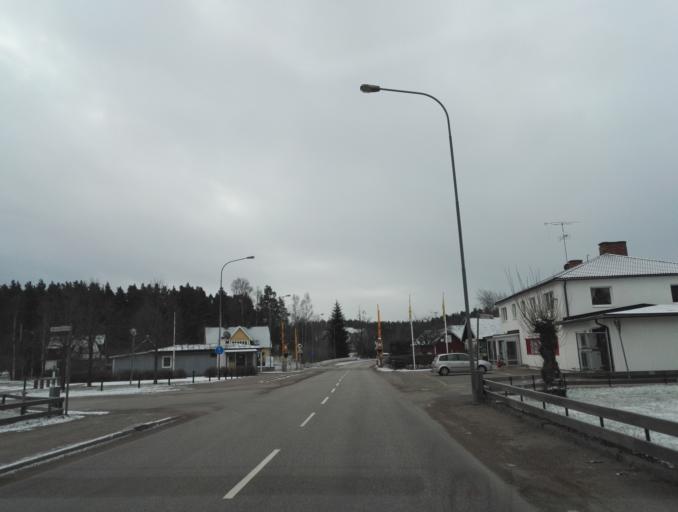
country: SE
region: Kalmar
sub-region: Hultsfreds Kommun
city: Virserum
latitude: 57.4078
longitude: 15.6184
